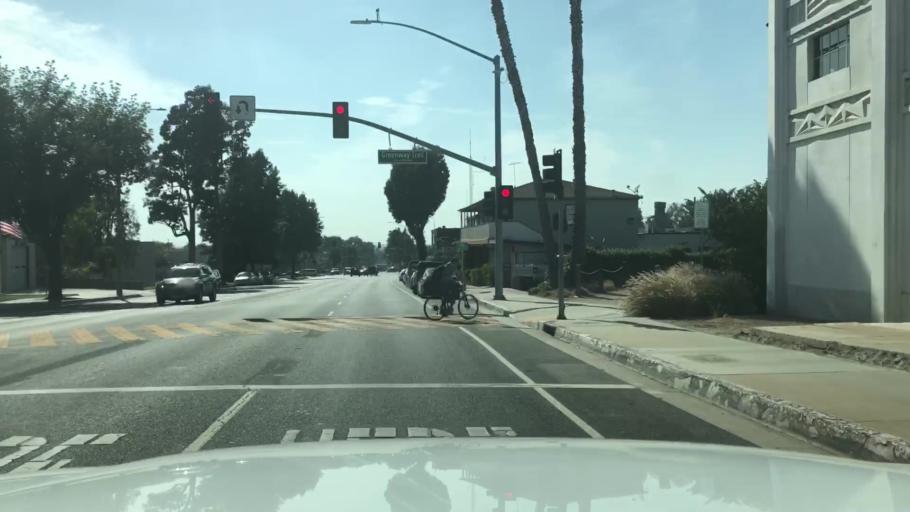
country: US
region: California
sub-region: Los Angeles County
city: Whittier
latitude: 33.9828
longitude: -118.0483
